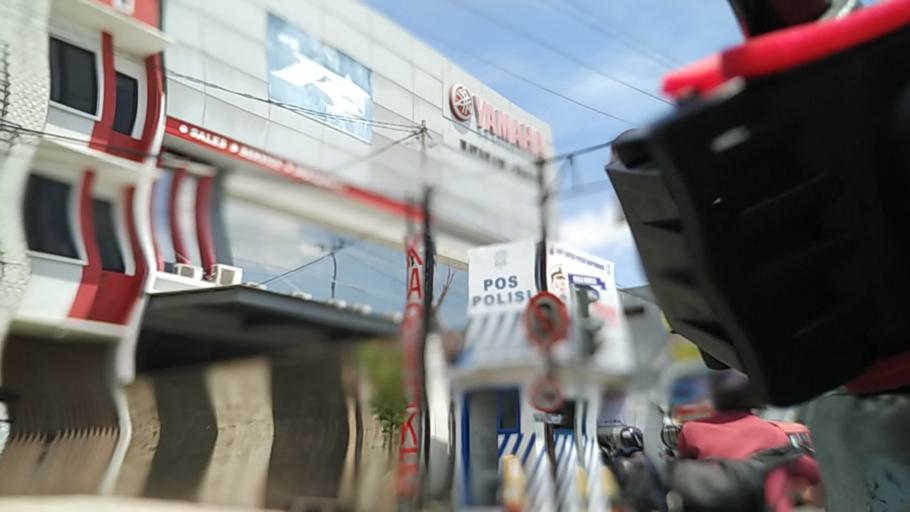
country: ID
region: Central Java
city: Semarang
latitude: -7.0485
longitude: 110.4198
